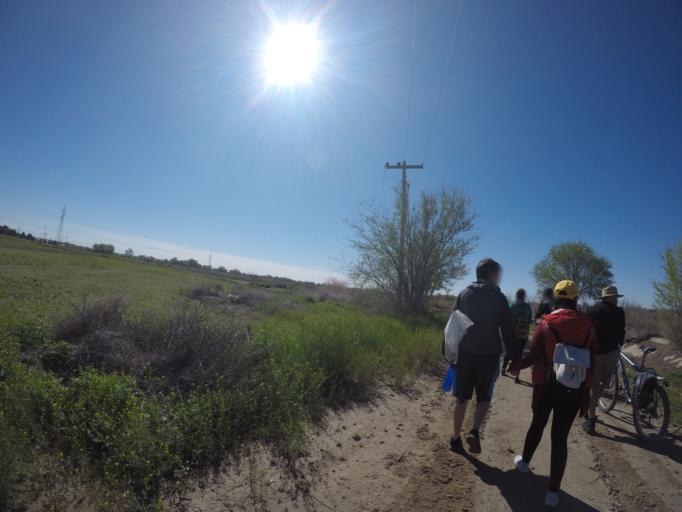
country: US
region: Texas
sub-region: El Paso County
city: Socorro
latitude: 31.6416
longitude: -106.3354
